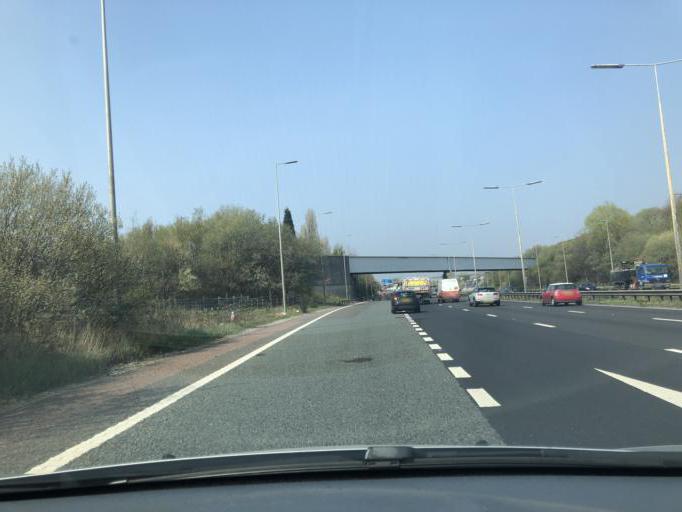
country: GB
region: England
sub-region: Borough of Tameside
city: Denton
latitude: 53.4511
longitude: -2.1358
